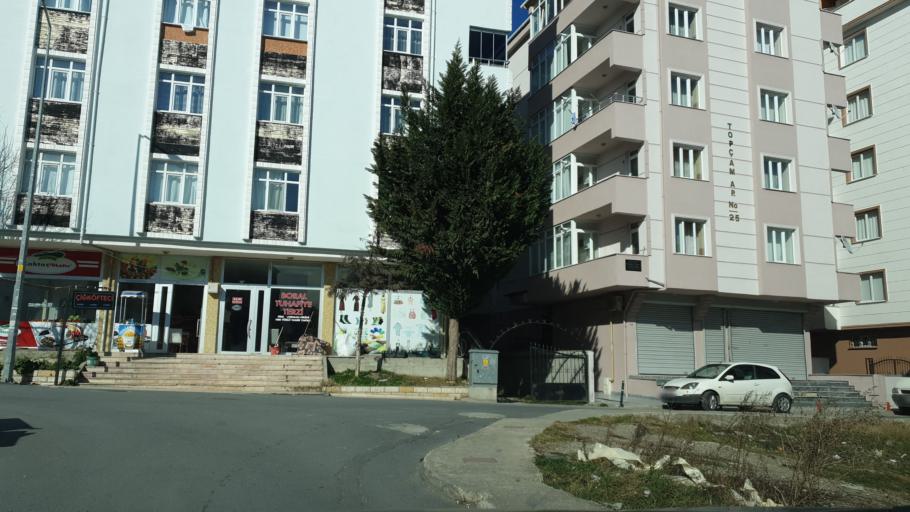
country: TR
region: Tekirdag
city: Cerkezkoey
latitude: 41.2857
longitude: 28.0088
